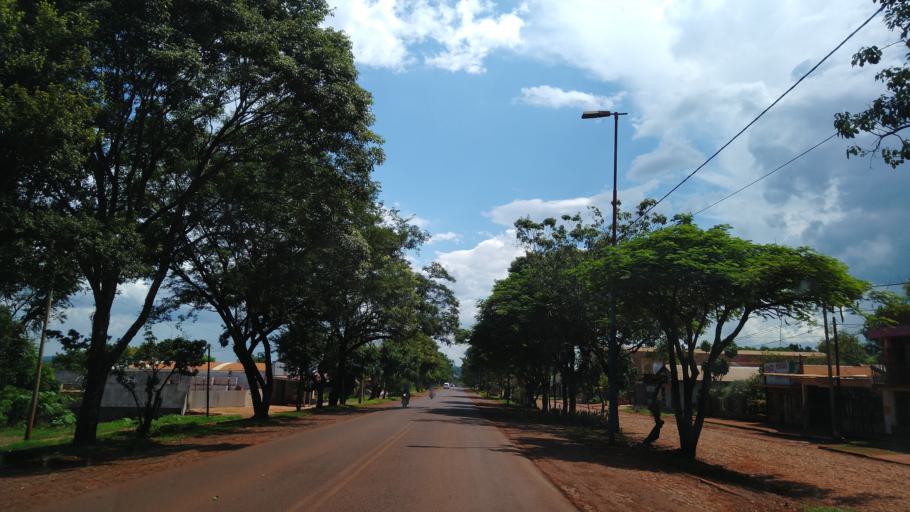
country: AR
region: Misiones
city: Puerto Libertad
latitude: -25.9703
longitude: -54.5731
